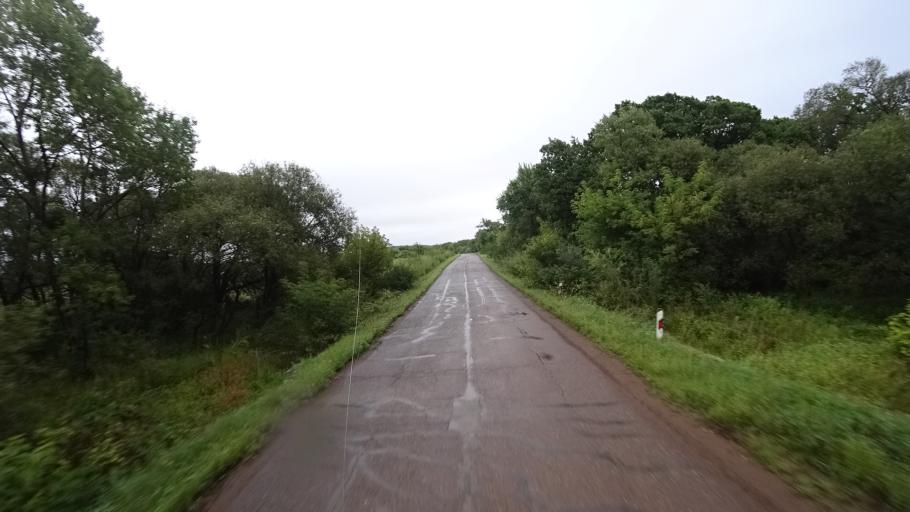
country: RU
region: Primorskiy
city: Monastyrishche
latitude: 44.2739
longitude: 132.4493
